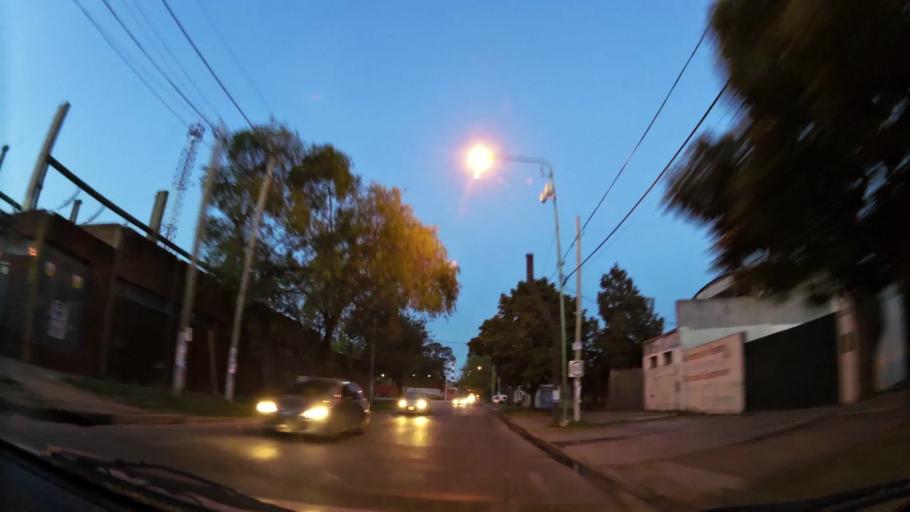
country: AR
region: Buenos Aires
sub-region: Partido de Quilmes
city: Quilmes
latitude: -34.7700
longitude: -58.2071
